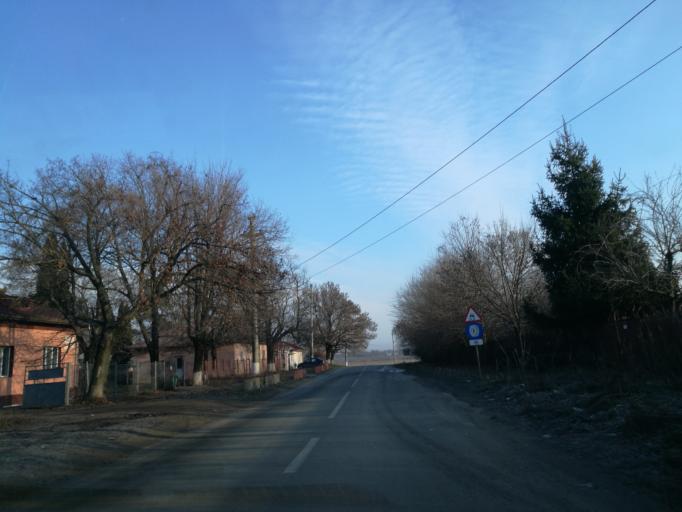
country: RO
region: Ialomita
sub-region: Comuna Fierbinti-Targ
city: Fierbintii de Jos
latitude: 44.6851
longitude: 26.3865
